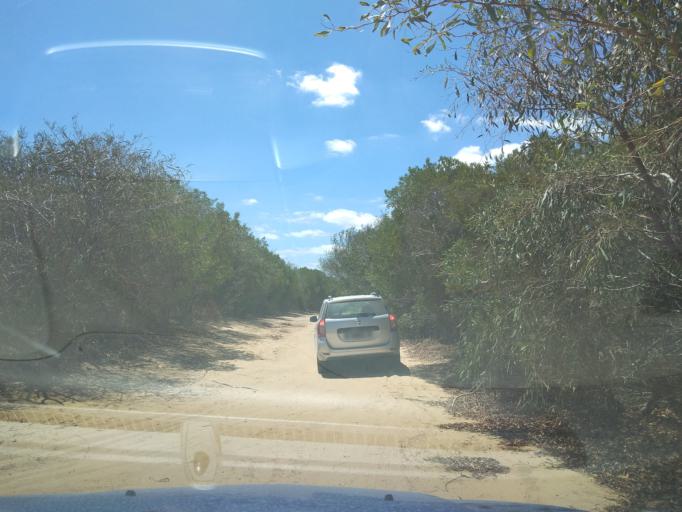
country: TN
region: Susah
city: Harqalah
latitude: 36.1605
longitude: 10.4639
